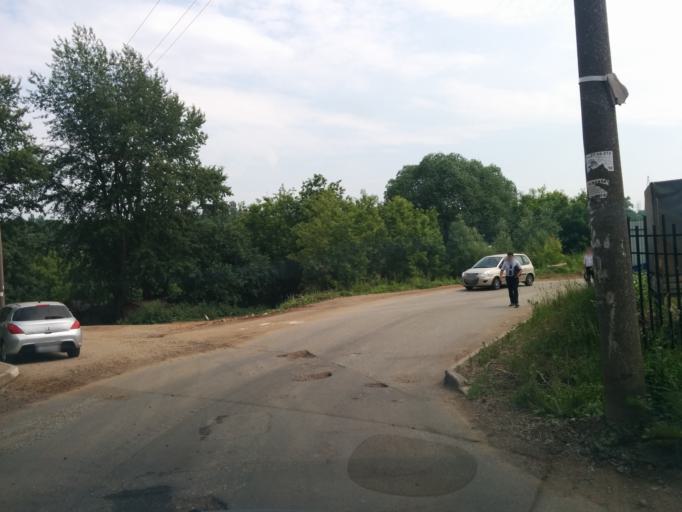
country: RU
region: Perm
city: Perm
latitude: 58.0153
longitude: 56.3031
